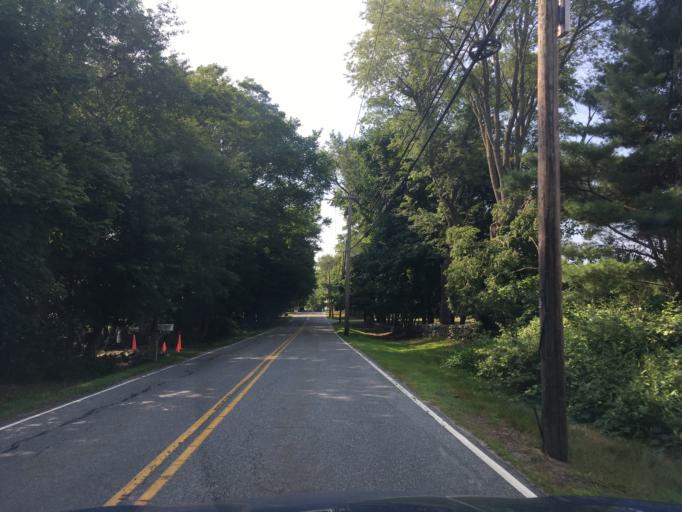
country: US
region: Rhode Island
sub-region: Kent County
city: East Greenwich
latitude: 41.6334
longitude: -71.4242
